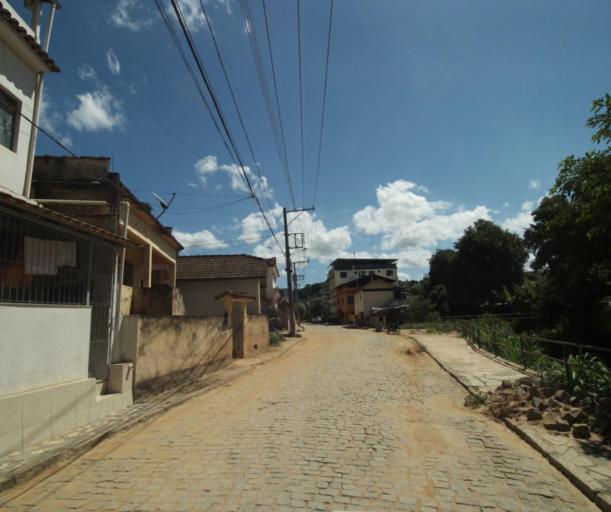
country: BR
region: Espirito Santo
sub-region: Mimoso Do Sul
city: Mimoso do Sul
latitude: -21.0613
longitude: -41.3588
